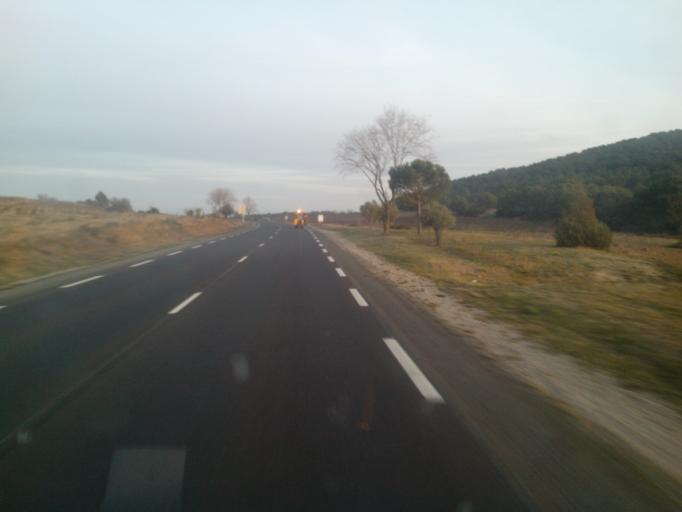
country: FR
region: Languedoc-Roussillon
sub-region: Departement de l'Herault
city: Olonzac
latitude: 43.2748
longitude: 2.7769
